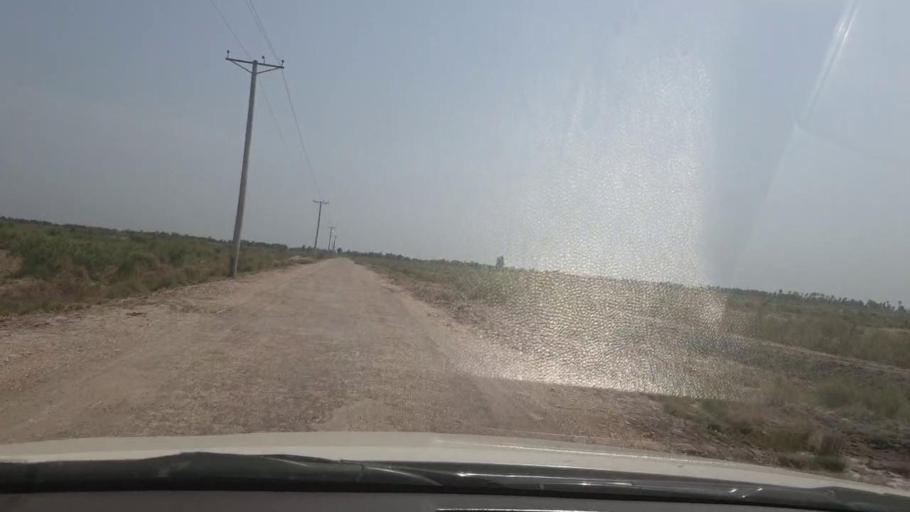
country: PK
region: Sindh
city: Garhi Yasin
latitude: 27.9852
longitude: 68.5021
